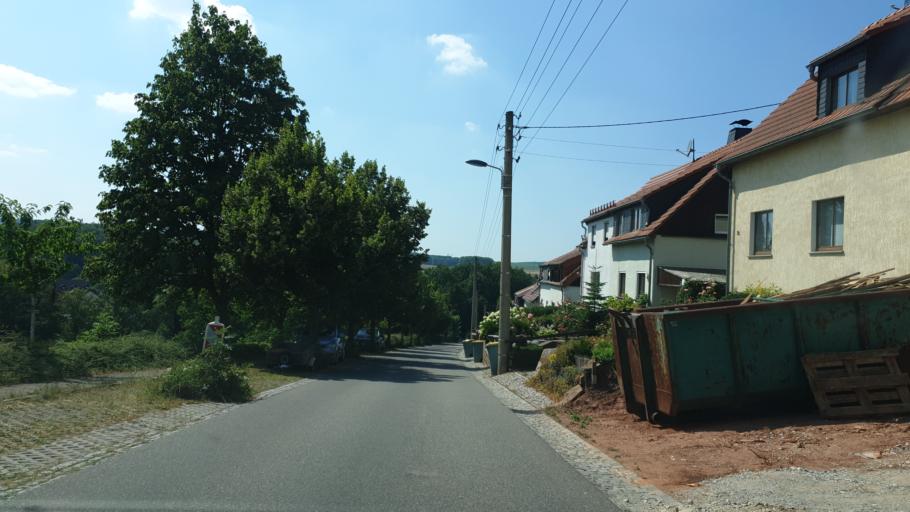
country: DE
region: Saxony
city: Gersdorf
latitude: 50.7511
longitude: 12.7161
